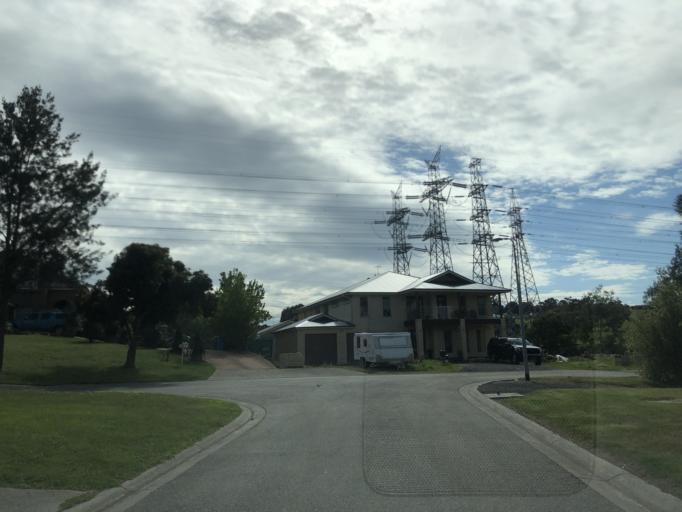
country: AU
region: Victoria
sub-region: Casey
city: Endeavour Hills
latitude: -37.9722
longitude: 145.2834
